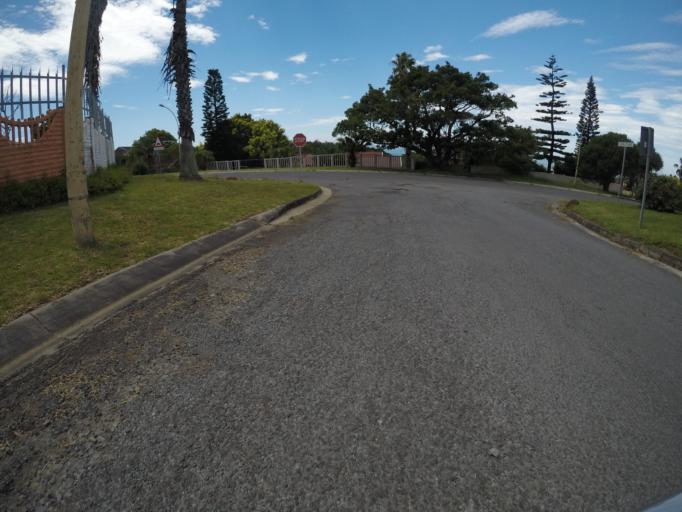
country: ZA
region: Eastern Cape
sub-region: Buffalo City Metropolitan Municipality
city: East London
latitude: -33.0374
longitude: 27.8634
